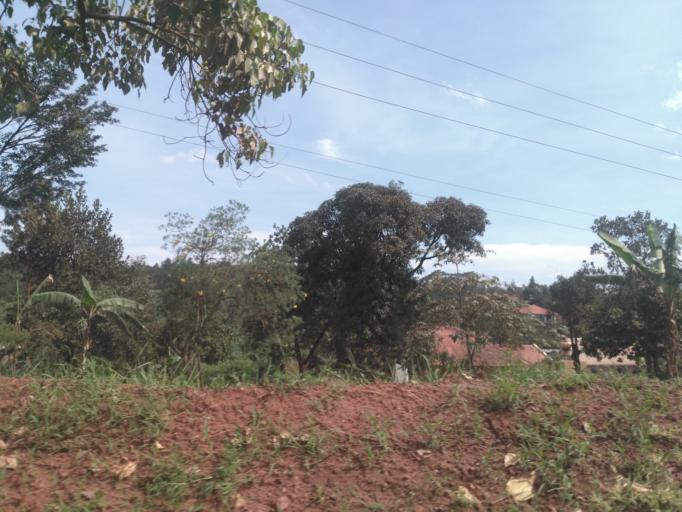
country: UG
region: Central Region
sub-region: Wakiso District
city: Kireka
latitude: 0.4419
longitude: 32.5874
